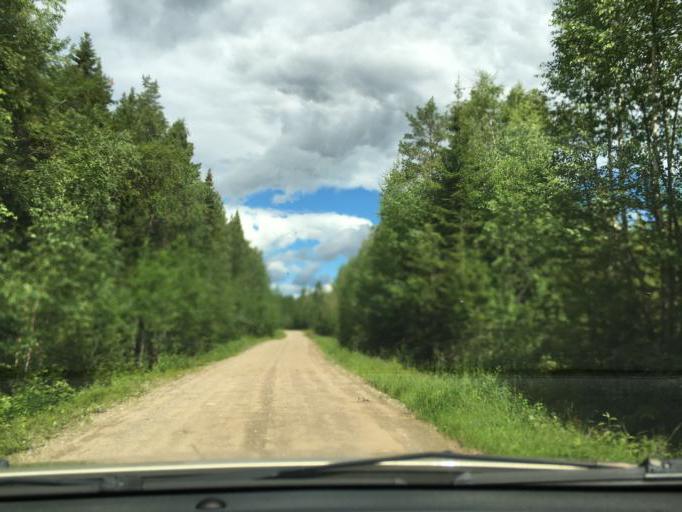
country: SE
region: Norrbotten
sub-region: Overkalix Kommun
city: OEverkalix
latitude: 66.1637
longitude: 22.8533
